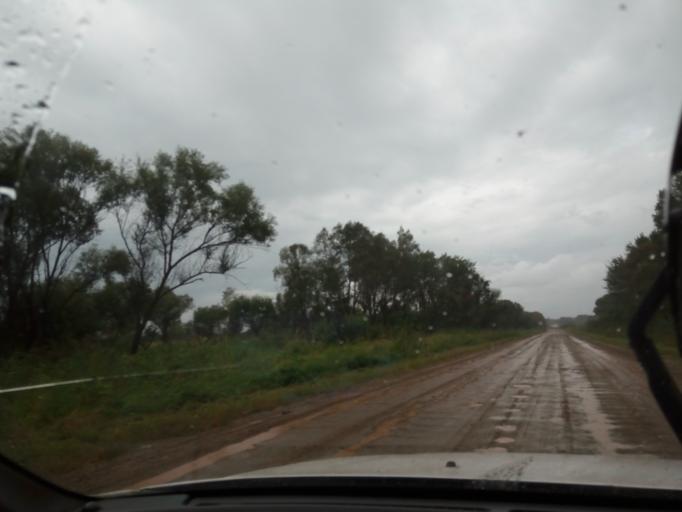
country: RU
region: Primorskiy
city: Lazo
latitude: 45.8481
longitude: 133.6453
